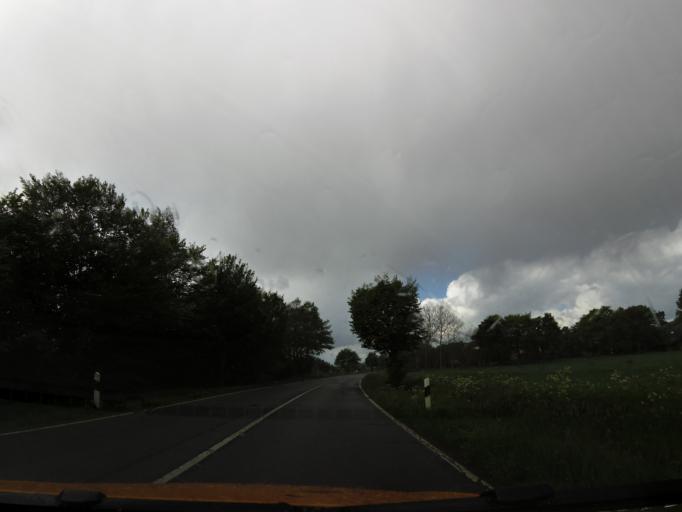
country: DE
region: Lower Saxony
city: Hude
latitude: 53.0923
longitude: 8.5044
